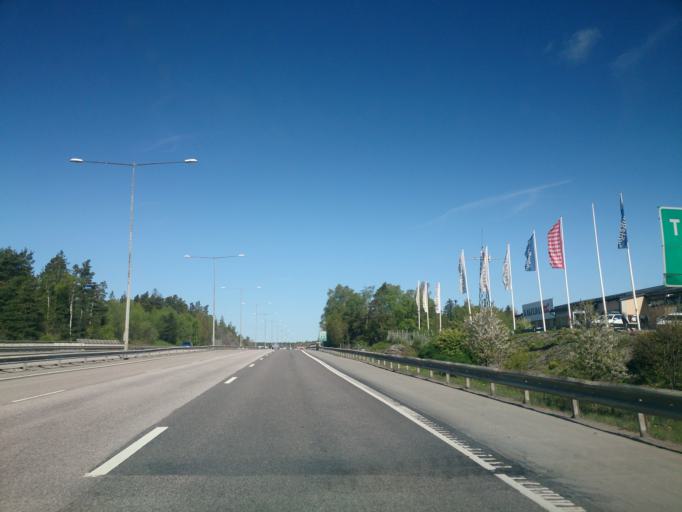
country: SE
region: Stockholm
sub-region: Haninge Kommun
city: Handen
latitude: 59.1924
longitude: 18.1411
